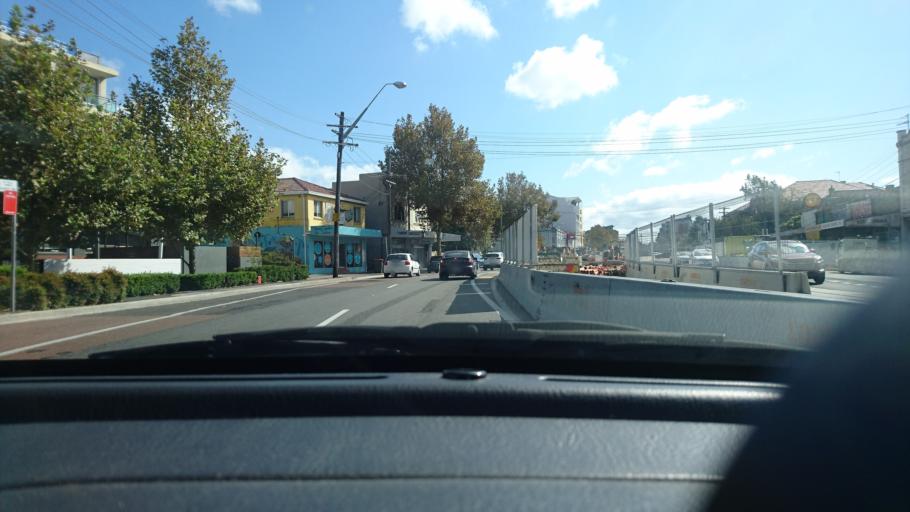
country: AU
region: New South Wales
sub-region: Randwick
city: Kensington
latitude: -33.9114
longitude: 151.2231
